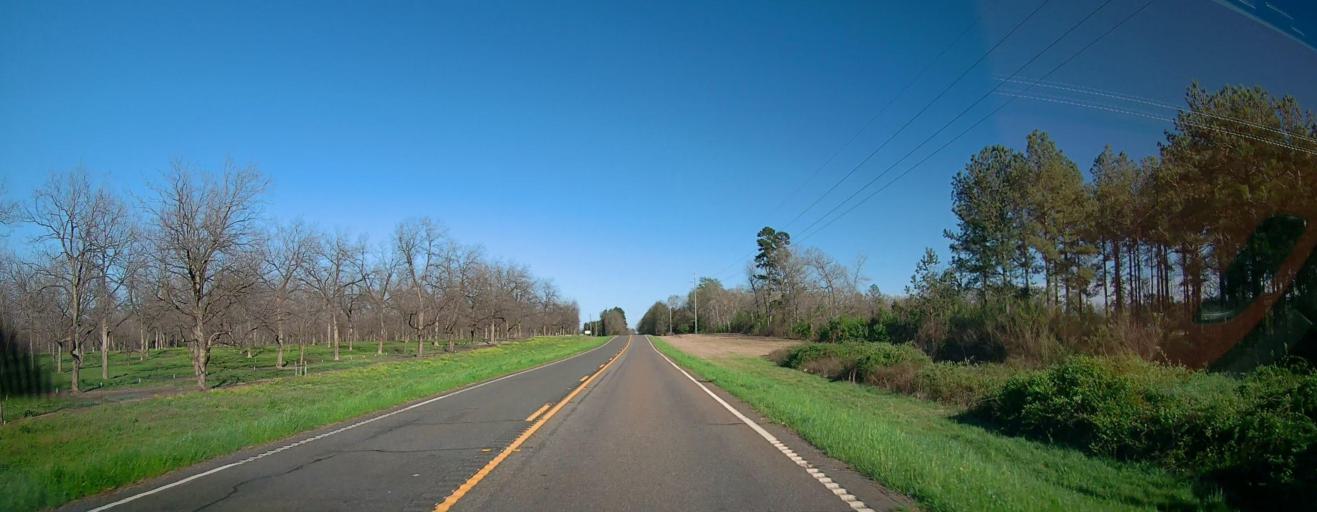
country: US
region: Georgia
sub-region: Macon County
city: Marshallville
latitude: 32.4394
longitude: -83.8589
